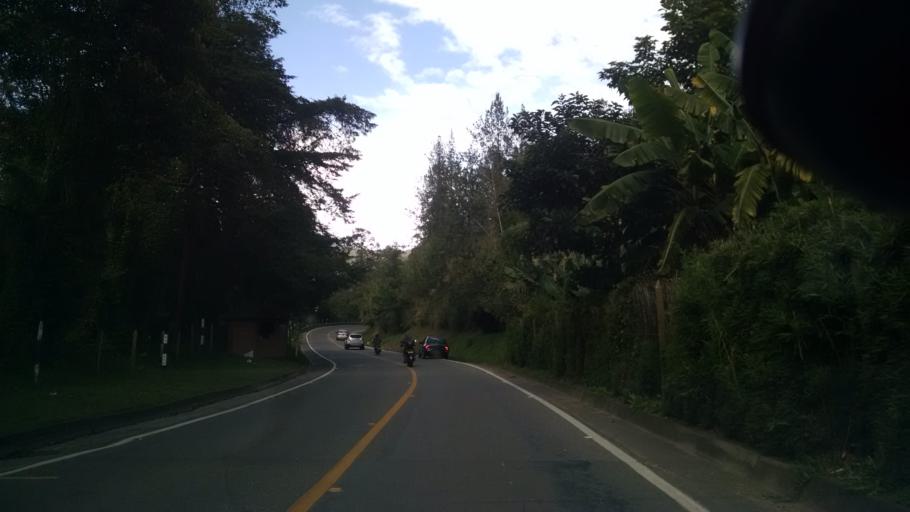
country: CO
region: Antioquia
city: El Retiro
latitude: 6.0870
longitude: -75.4919
